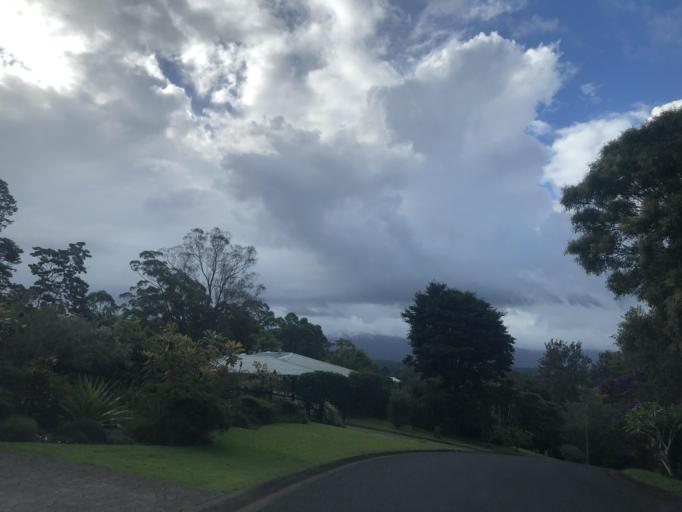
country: AU
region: New South Wales
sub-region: Bellingen
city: Bellingen
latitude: -30.4599
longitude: 152.9014
